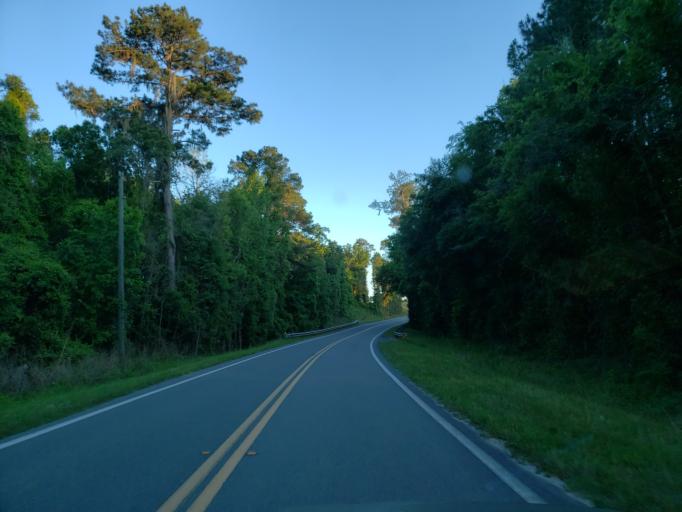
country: US
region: Florida
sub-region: Madison County
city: Madison
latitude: 30.6080
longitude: -83.2544
